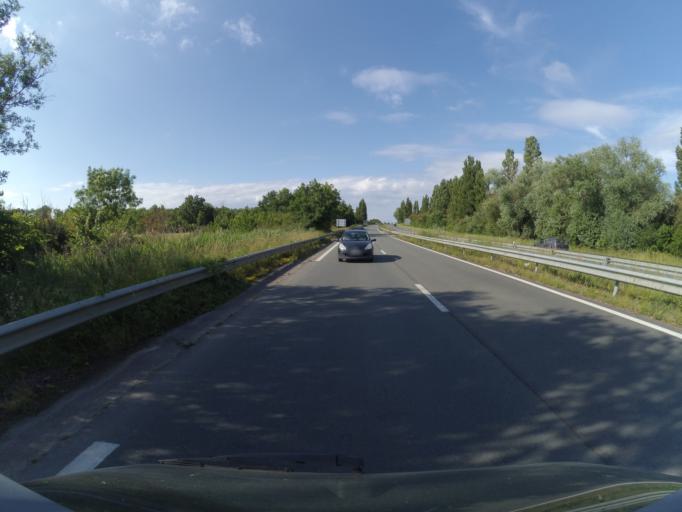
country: FR
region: Poitou-Charentes
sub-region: Departement de la Charente-Maritime
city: Saint-Agnant
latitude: 45.8715
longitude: -0.9689
